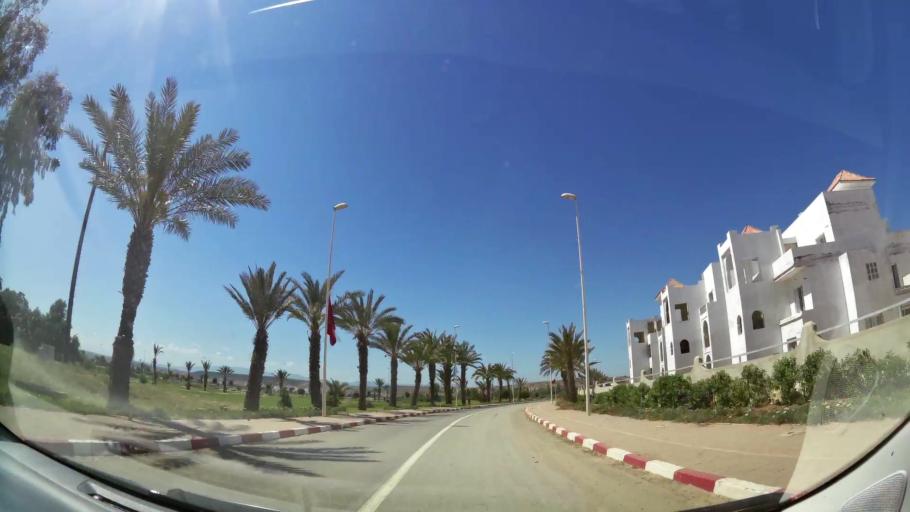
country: MA
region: Oriental
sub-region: Berkane-Taourirt
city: Madagh
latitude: 35.1094
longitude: -2.3107
